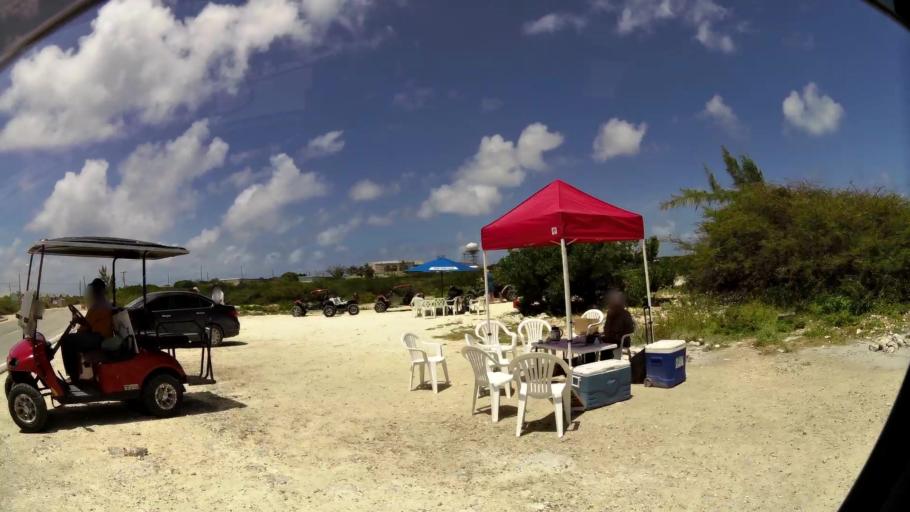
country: TC
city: Cockburn Town
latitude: 21.4300
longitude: -71.1438
